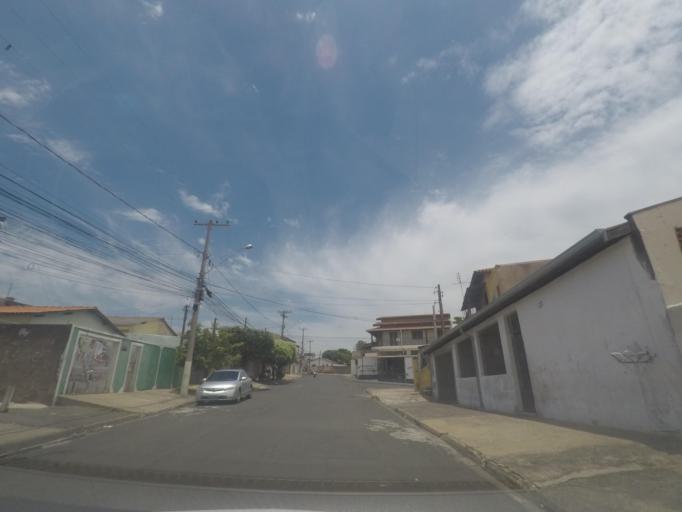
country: BR
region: Sao Paulo
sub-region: Nova Odessa
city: Nova Odessa
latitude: -22.7941
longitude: -47.2783
